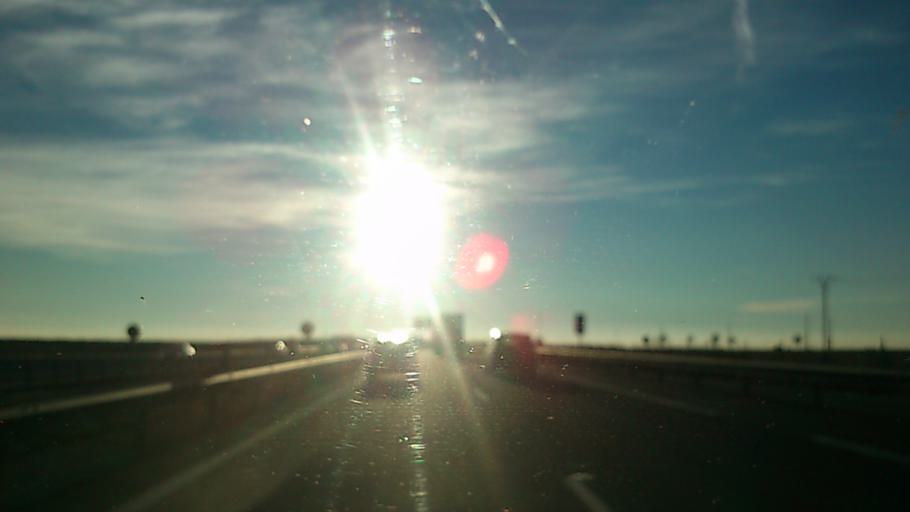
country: ES
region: Castille-La Mancha
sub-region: Provincia de Guadalajara
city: Muduex
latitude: 40.8103
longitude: -2.9405
